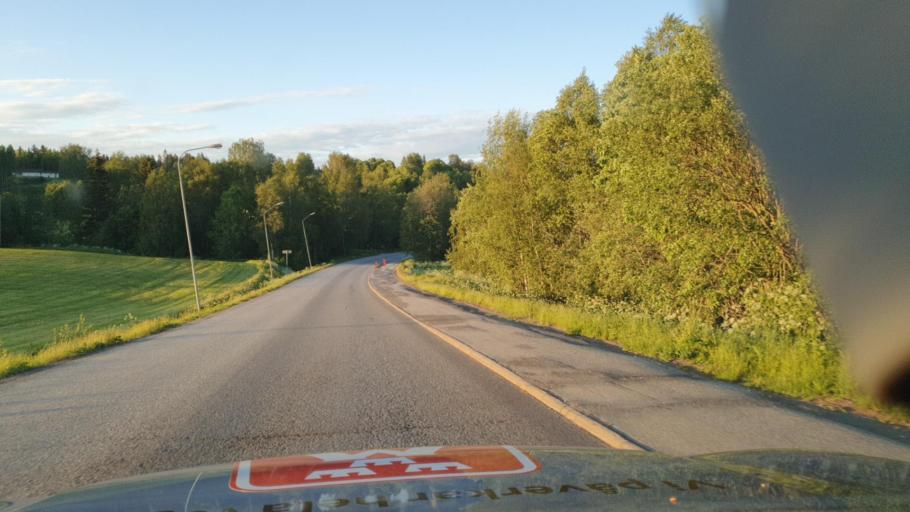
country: SE
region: Vaesternorrland
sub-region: OErnskoeldsviks Kommun
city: Bjasta
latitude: 63.2846
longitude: 18.5400
